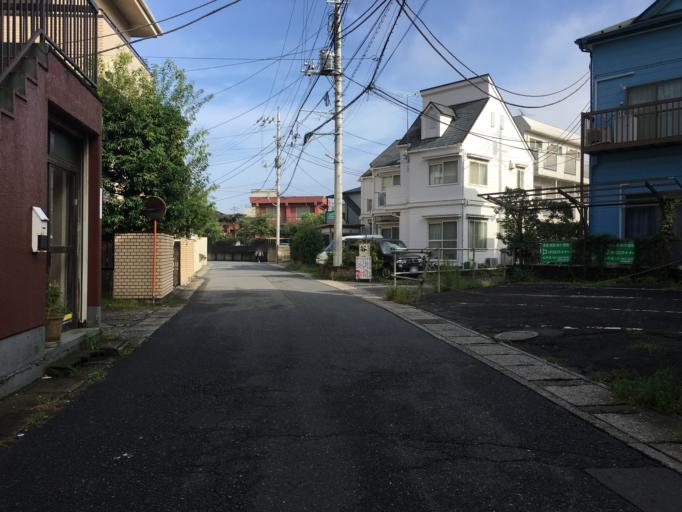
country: JP
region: Chiba
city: Matsudo
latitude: 35.7892
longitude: 139.9002
